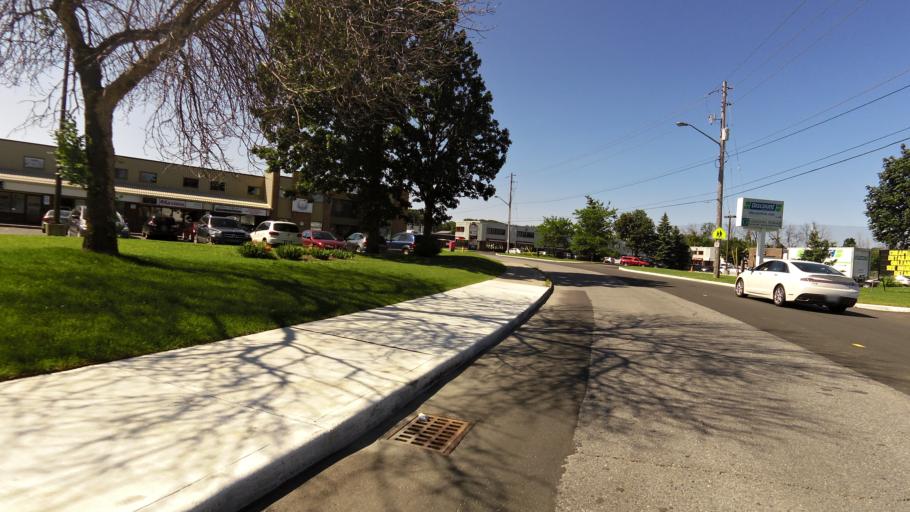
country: CA
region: Quebec
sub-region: Outaouais
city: Gatineau
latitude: 45.4646
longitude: -75.5502
